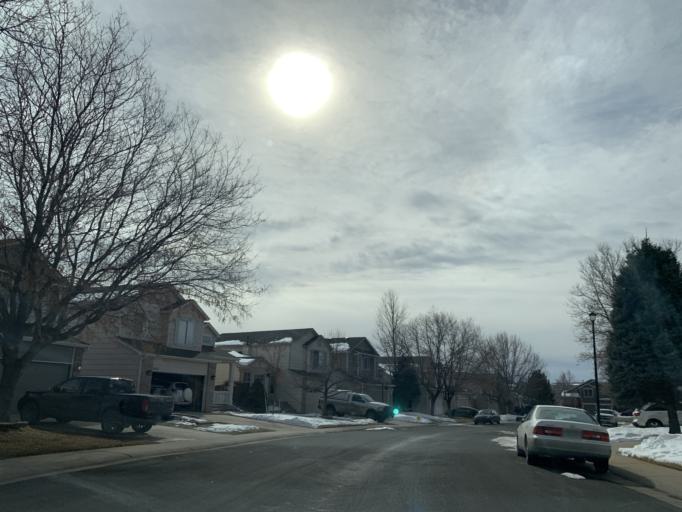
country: US
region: Colorado
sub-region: Douglas County
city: Carriage Club
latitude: 39.5406
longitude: -104.9286
